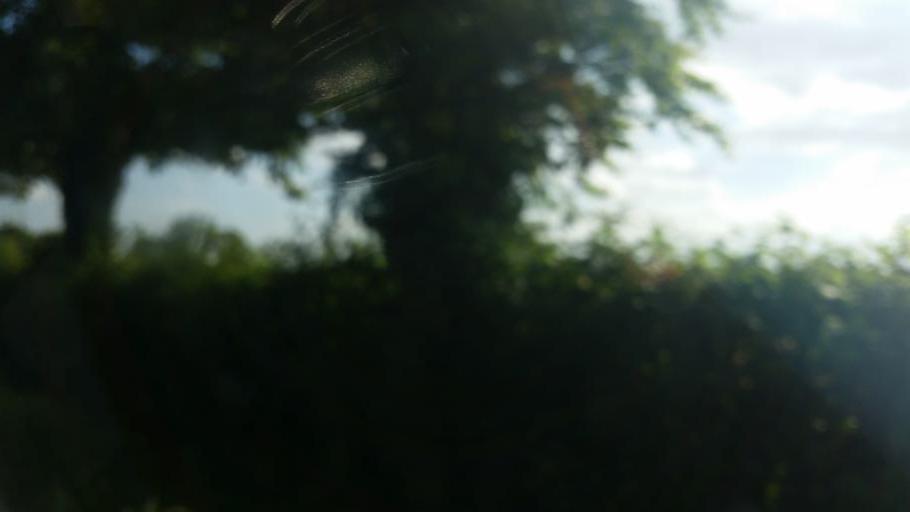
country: IE
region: Leinster
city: Hartstown
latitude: 53.4333
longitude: -6.4283
